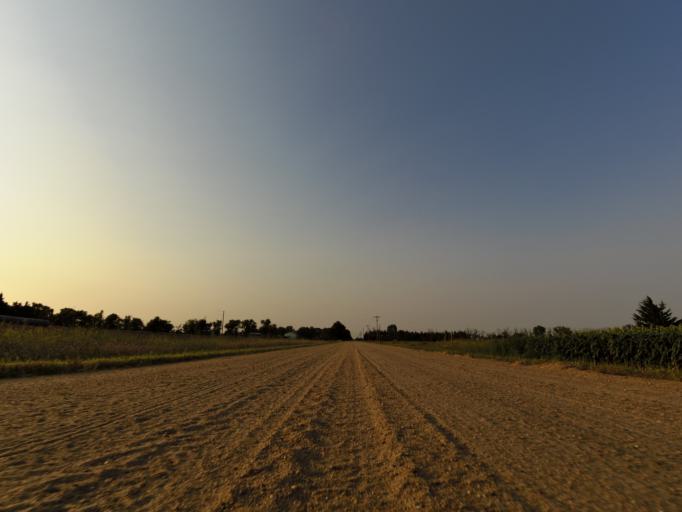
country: US
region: Kansas
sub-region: Reno County
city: South Hutchinson
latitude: 37.9833
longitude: -97.9958
